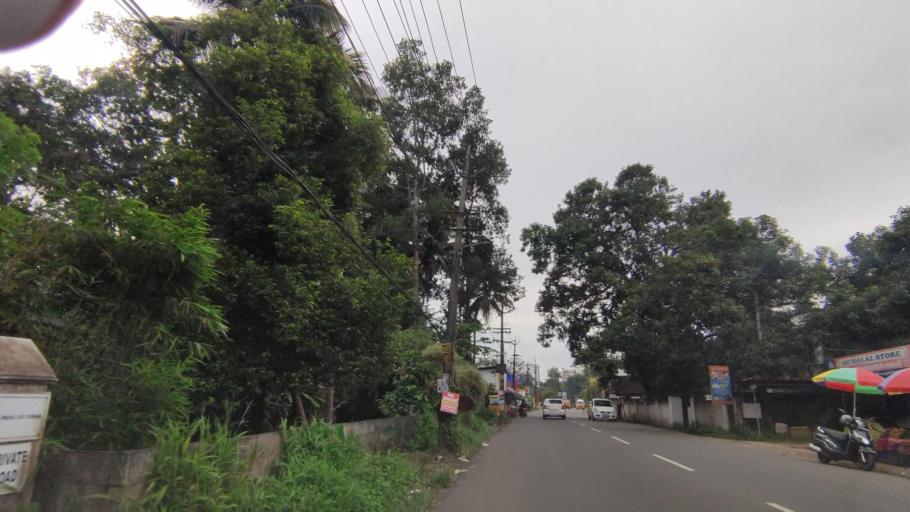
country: IN
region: Kerala
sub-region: Kottayam
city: Kottayam
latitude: 9.6041
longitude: 76.5158
